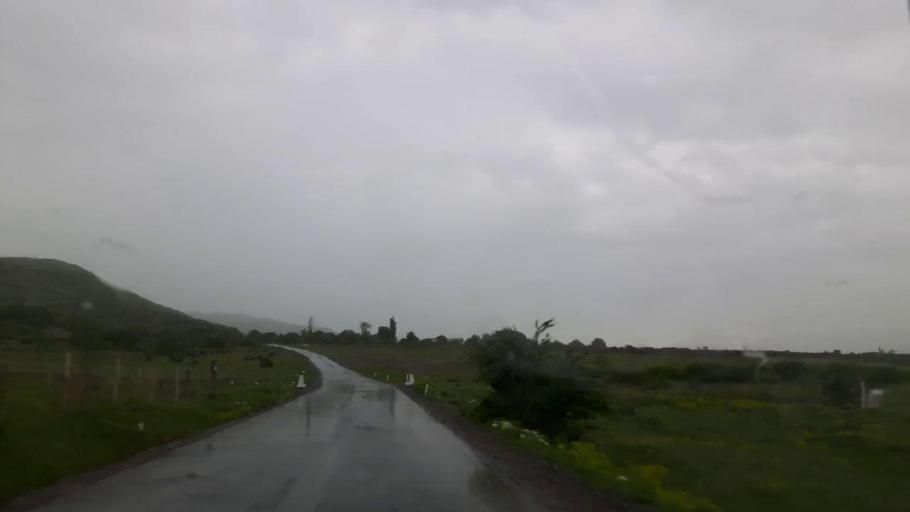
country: GE
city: Agara
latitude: 41.9820
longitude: 43.9475
